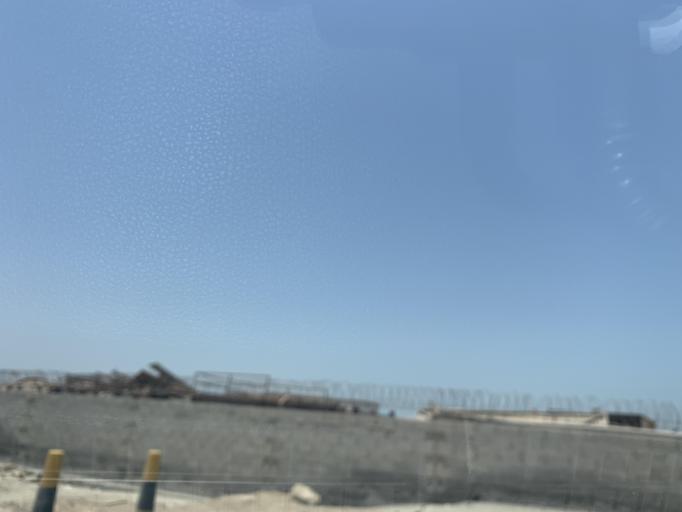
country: BH
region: Muharraq
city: Al Muharraq
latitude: 26.2843
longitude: 50.6177
